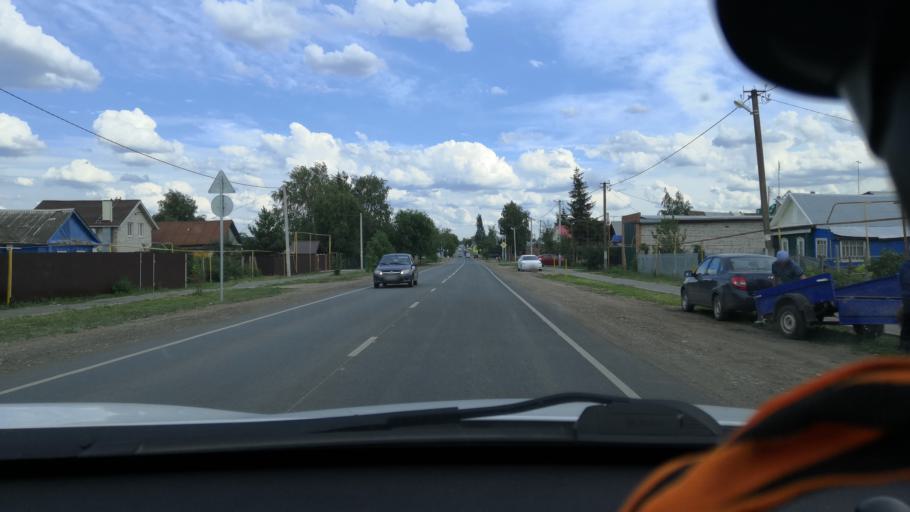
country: RU
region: Samara
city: Novosemeykino
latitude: 53.3801
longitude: 50.3420
